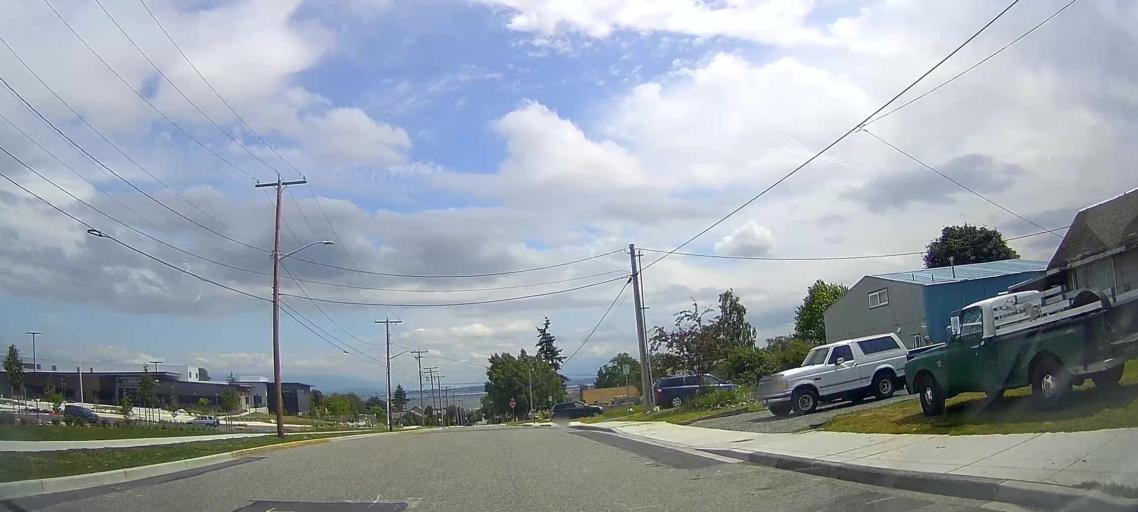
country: US
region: Washington
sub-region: Skagit County
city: Anacortes
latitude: 48.5062
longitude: -122.6221
